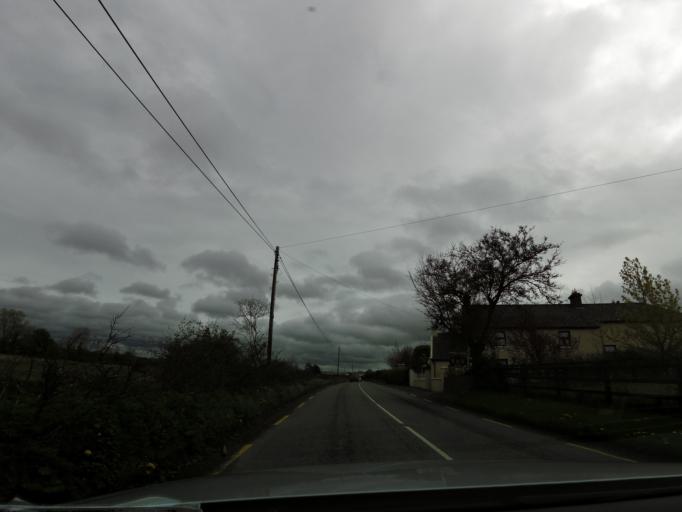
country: IE
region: Leinster
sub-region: Kilkenny
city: Ballyragget
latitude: 52.7305
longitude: -7.3872
